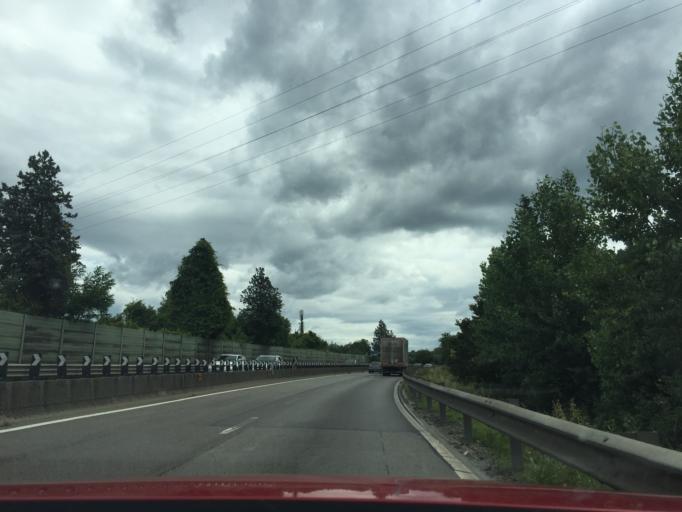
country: IT
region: Tuscany
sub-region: Province of Florence
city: Montelupo Fiorentino
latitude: 43.7247
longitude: 11.0148
